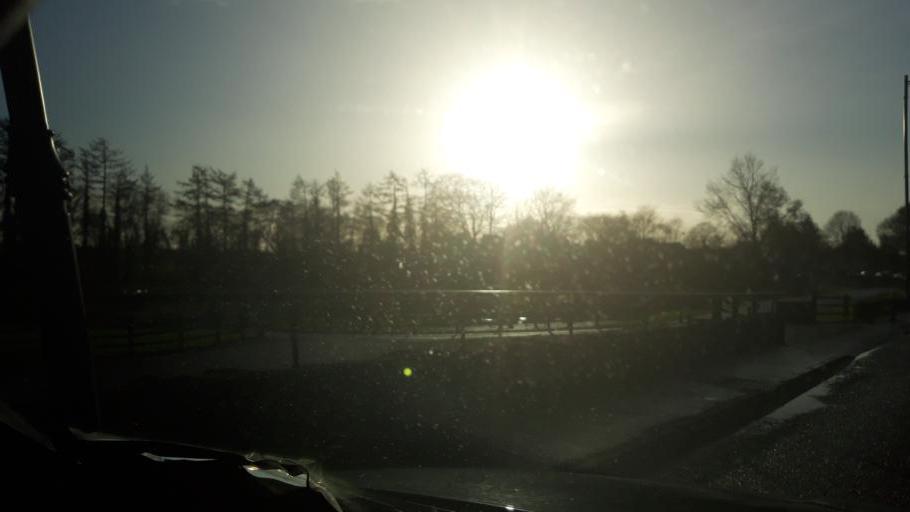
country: GB
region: Northern Ireland
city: Maghera
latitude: 54.9084
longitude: -6.6659
